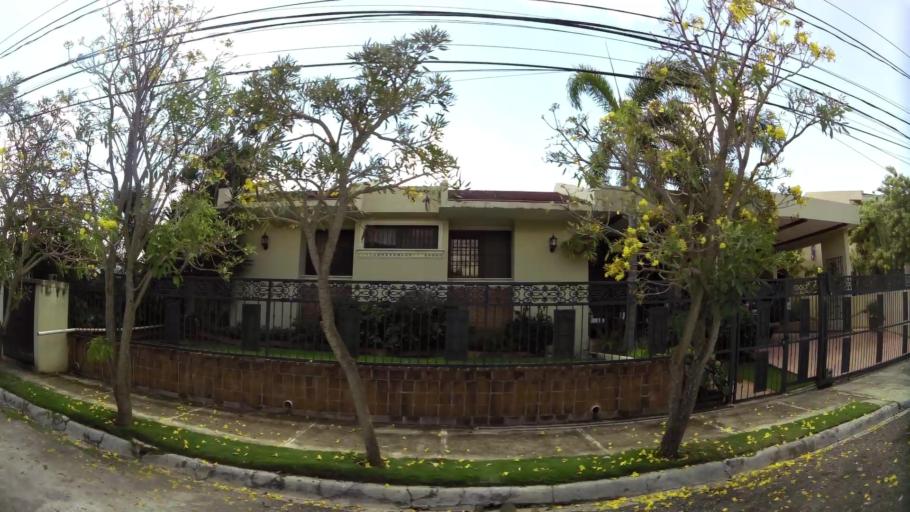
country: DO
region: Santiago
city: Santiago de los Caballeros
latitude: 19.4713
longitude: -70.6755
